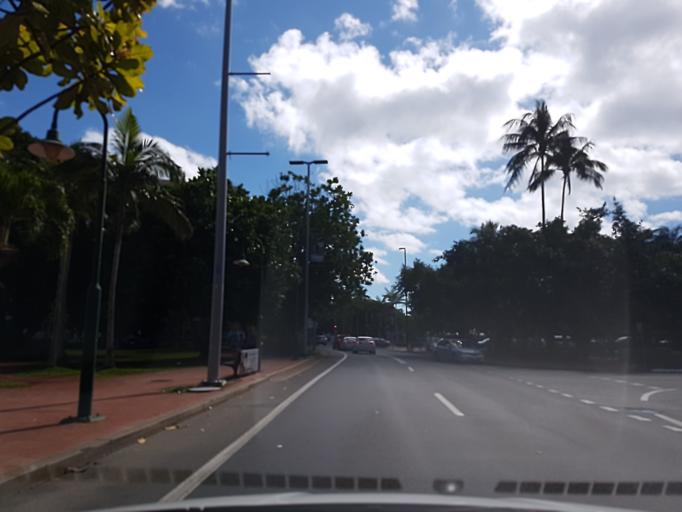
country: AU
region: Queensland
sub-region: Cairns
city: Cairns
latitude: -16.9229
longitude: 145.7797
